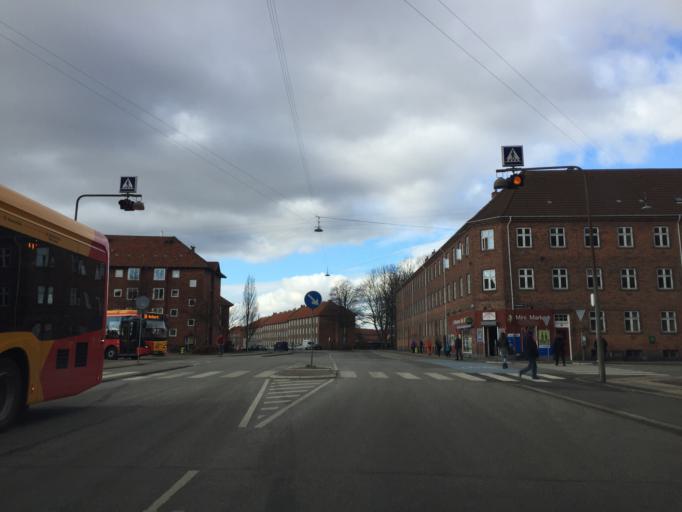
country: DK
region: Capital Region
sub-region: Frederiksberg Kommune
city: Frederiksberg
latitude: 55.6489
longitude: 12.5349
